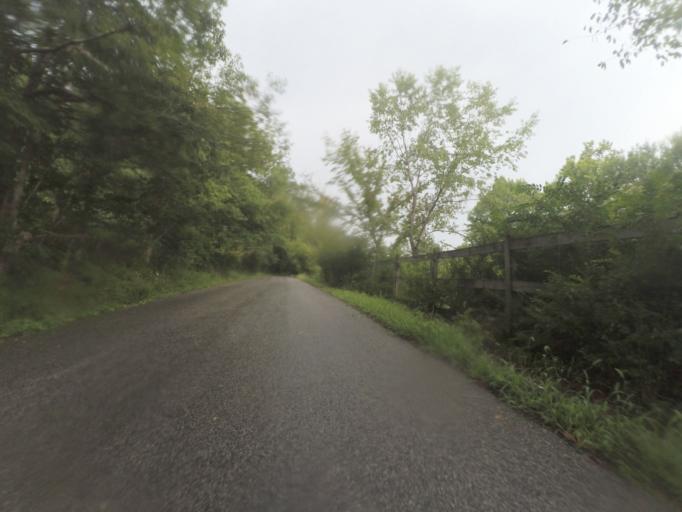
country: US
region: West Virginia
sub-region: Cabell County
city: Huntington
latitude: 38.3778
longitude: -82.4002
